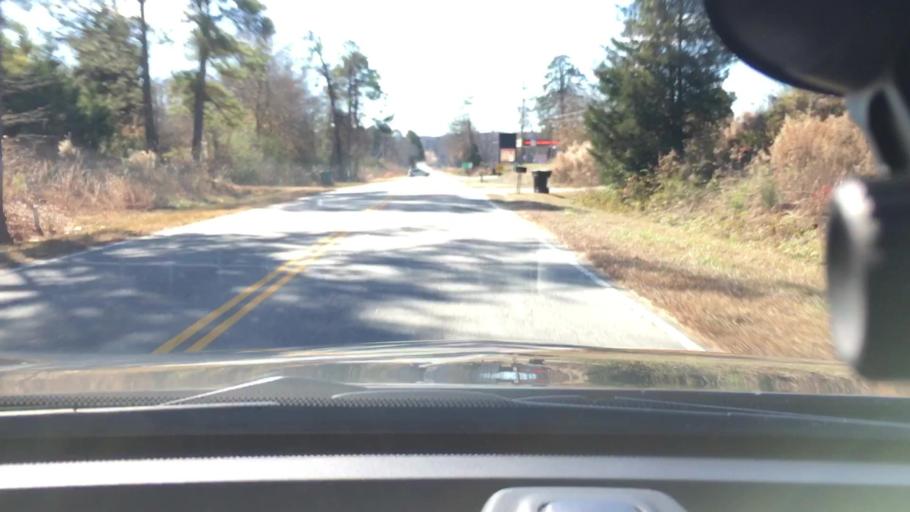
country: US
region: South Carolina
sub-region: Cherokee County
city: Gaffney
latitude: 34.9830
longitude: -81.6957
